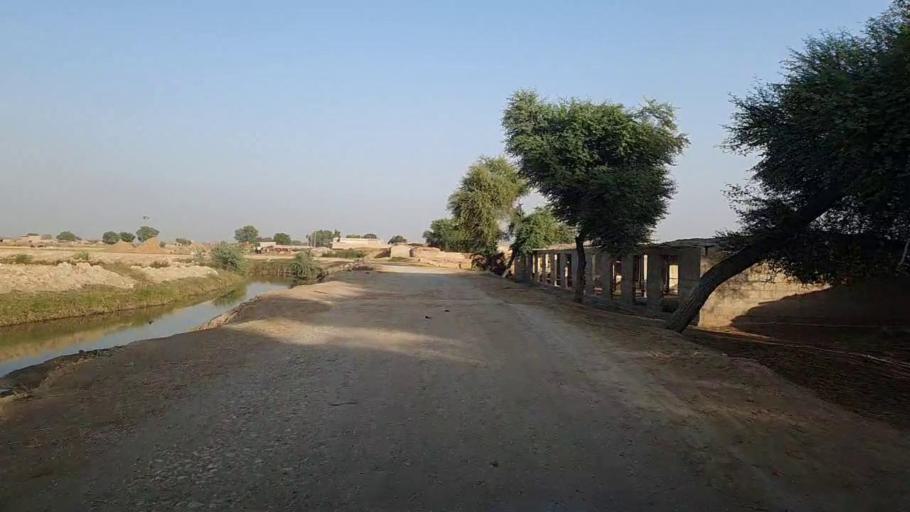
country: PK
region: Sindh
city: Kashmor
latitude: 28.4270
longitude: 69.4415
